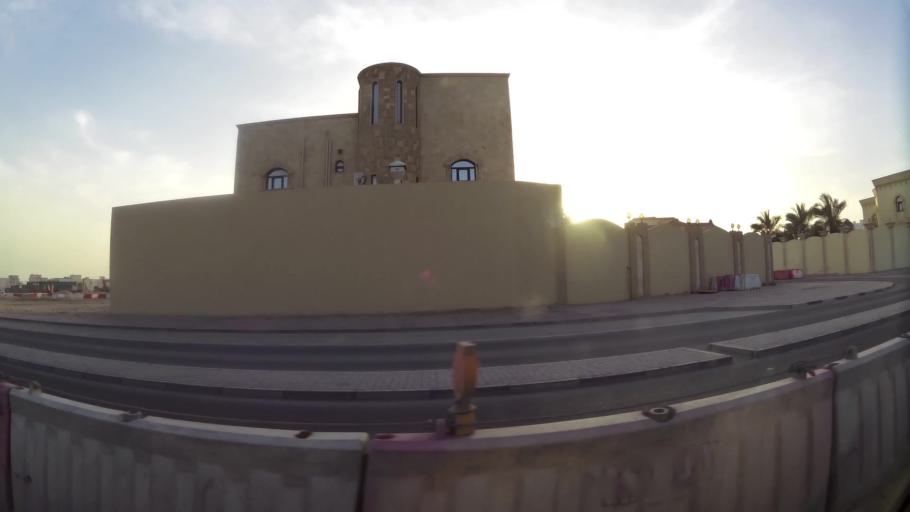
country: QA
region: Al Wakrah
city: Al Wakrah
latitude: 25.1530
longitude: 51.5933
